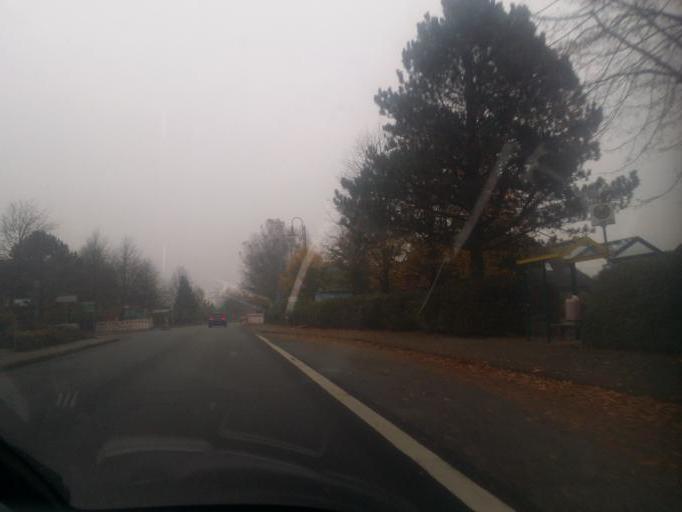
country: DE
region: Schleswig-Holstein
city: Tarp
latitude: 54.6669
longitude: 9.4077
